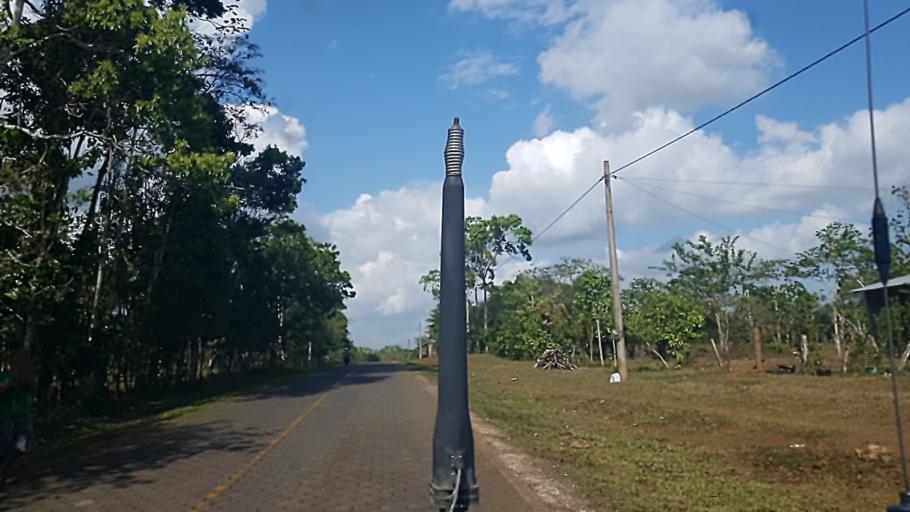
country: NI
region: Atlantico Sur
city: Nueva Guinea
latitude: 11.6972
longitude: -84.3907
